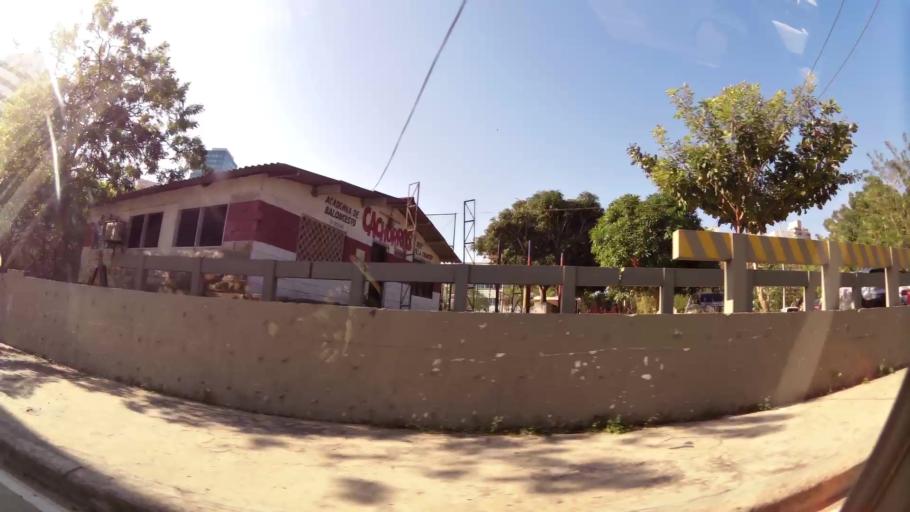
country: CO
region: Atlantico
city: Barranquilla
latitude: 11.0087
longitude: -74.8040
